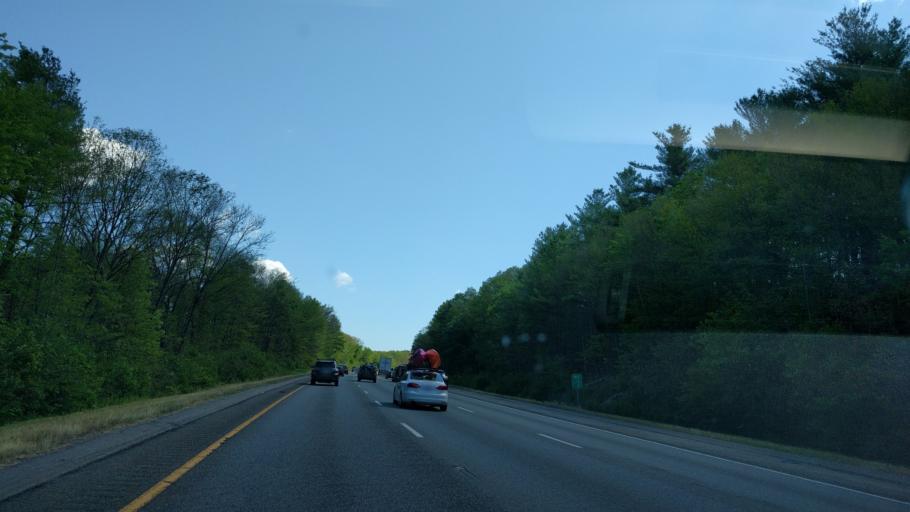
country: US
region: Massachusetts
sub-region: Worcester County
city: Shrewsbury
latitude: 42.3141
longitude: -71.7286
